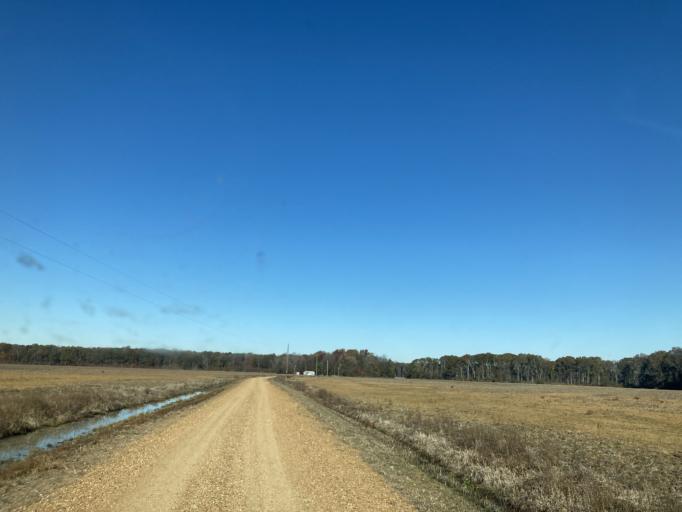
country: US
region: Mississippi
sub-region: Sharkey County
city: Rolling Fork
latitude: 32.9019
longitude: -90.6652
